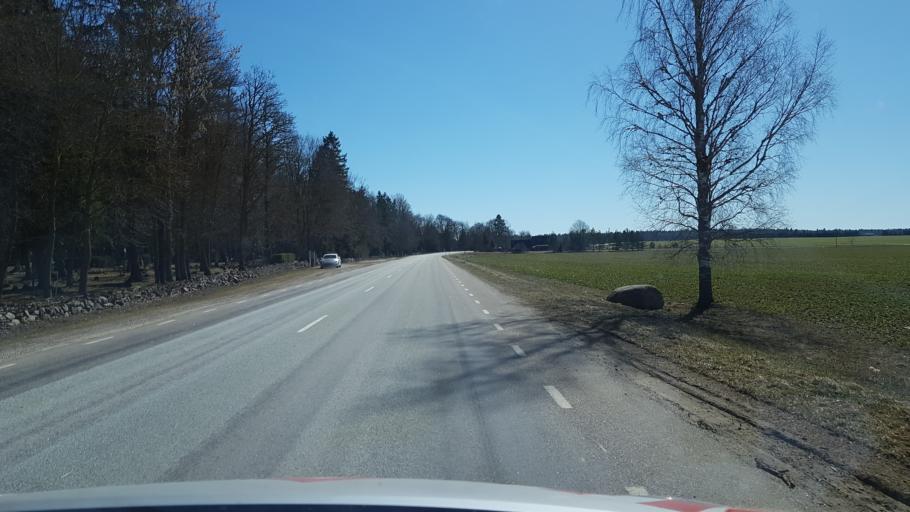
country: EE
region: Laeaene-Virumaa
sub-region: Viru-Nigula vald
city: Kunda
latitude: 59.4390
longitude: 26.6975
